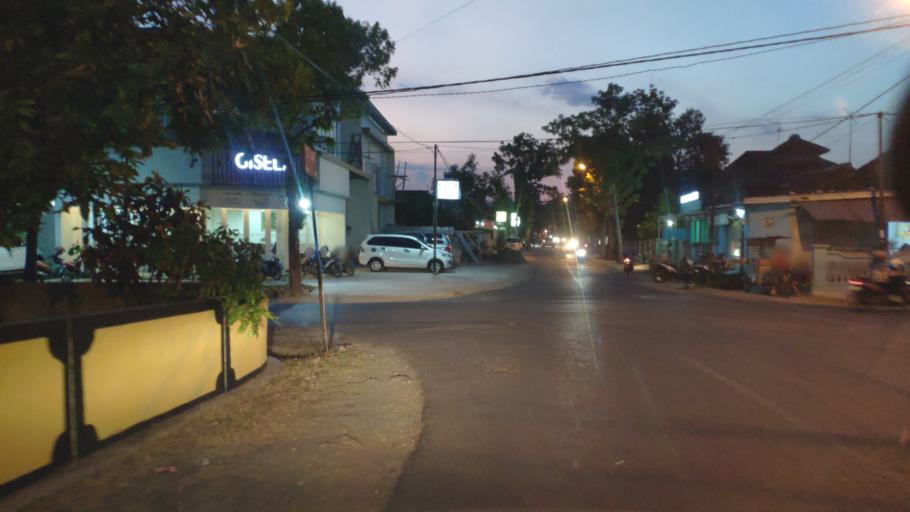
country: ID
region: Central Java
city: Tempelan
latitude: -6.9646
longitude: 111.4184
